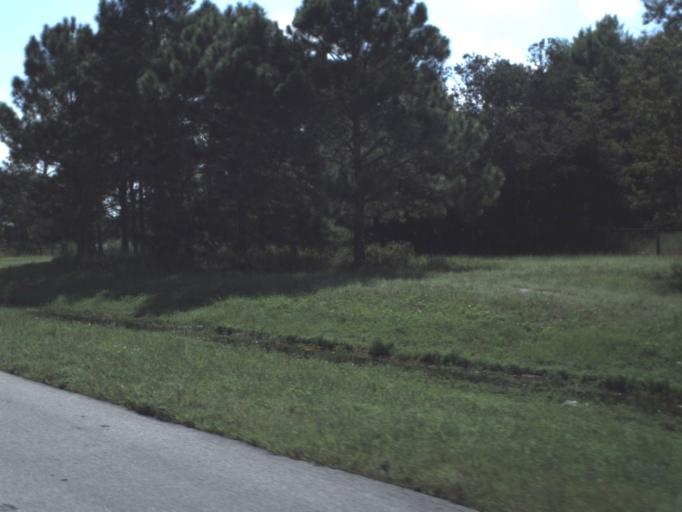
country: US
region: Florida
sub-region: Polk County
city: Polk City
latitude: 28.1565
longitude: -81.8379
